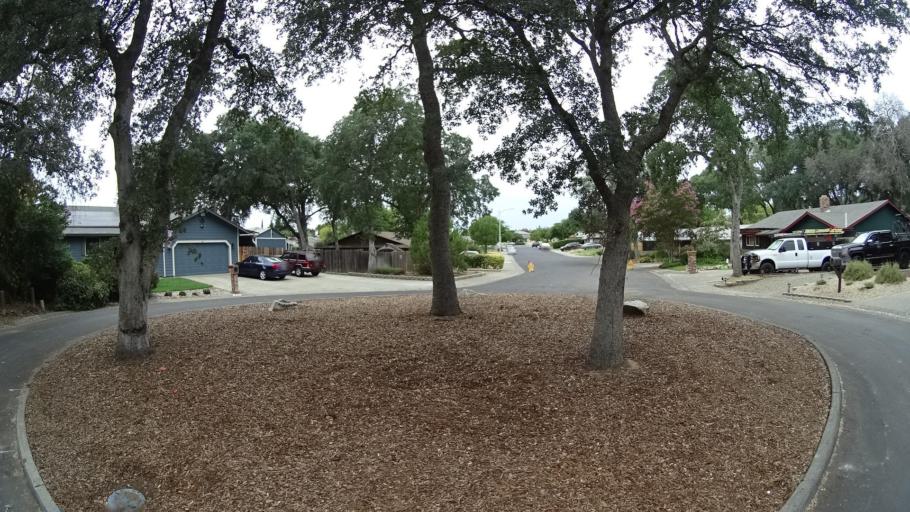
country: US
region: California
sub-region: Placer County
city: Rocklin
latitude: 38.7758
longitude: -121.2410
